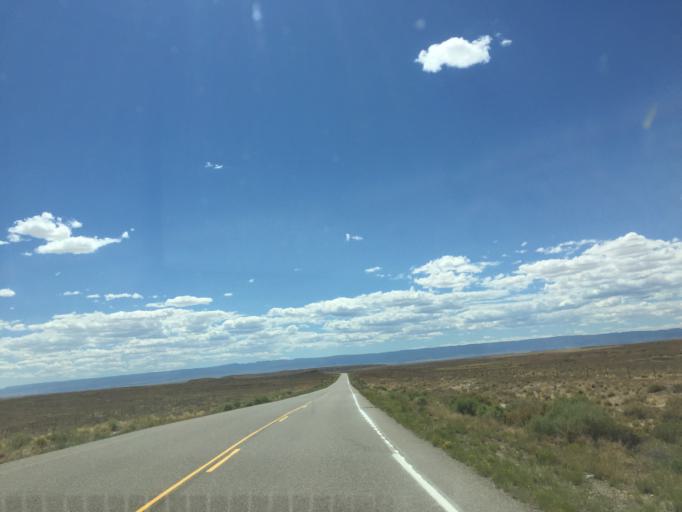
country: US
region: New Mexico
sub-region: San Juan County
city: Kirtland
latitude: 36.3845
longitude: -108.4880
